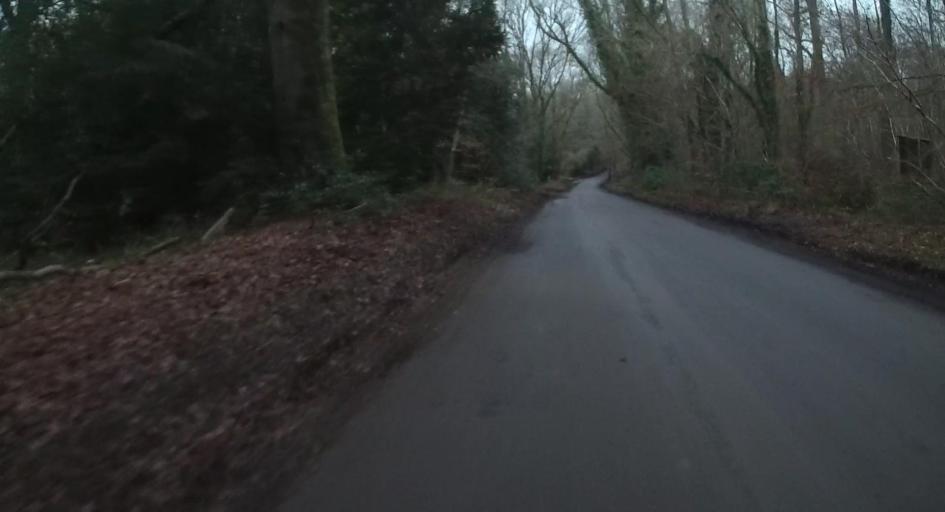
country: GB
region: England
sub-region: Hampshire
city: Four Marks
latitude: 51.0583
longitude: -1.1006
